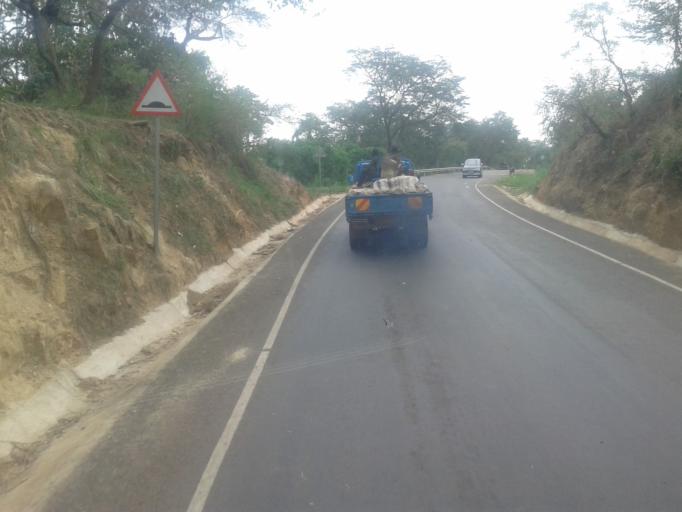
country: UG
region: Northern Region
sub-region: Oyam District
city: Oyam
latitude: 2.2437
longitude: 32.2395
